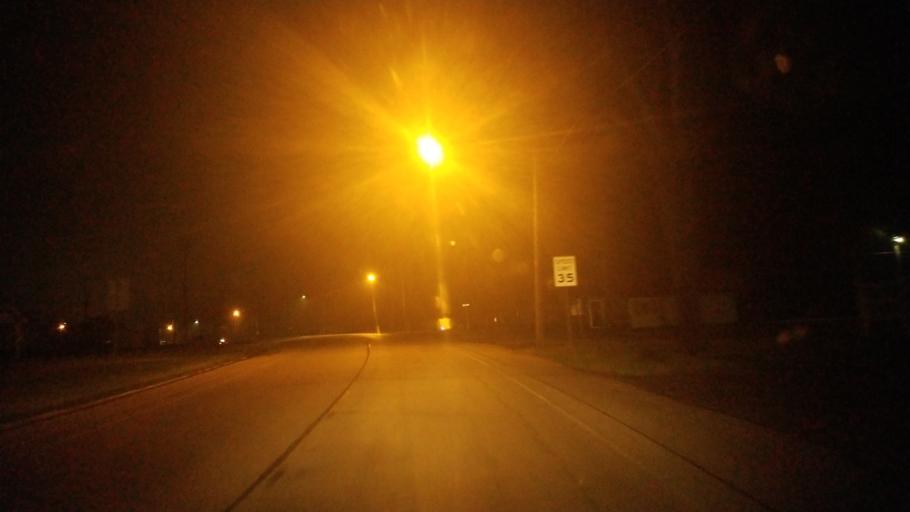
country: US
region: Missouri
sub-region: Pike County
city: Bowling Green
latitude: 39.3436
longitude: -91.2028
